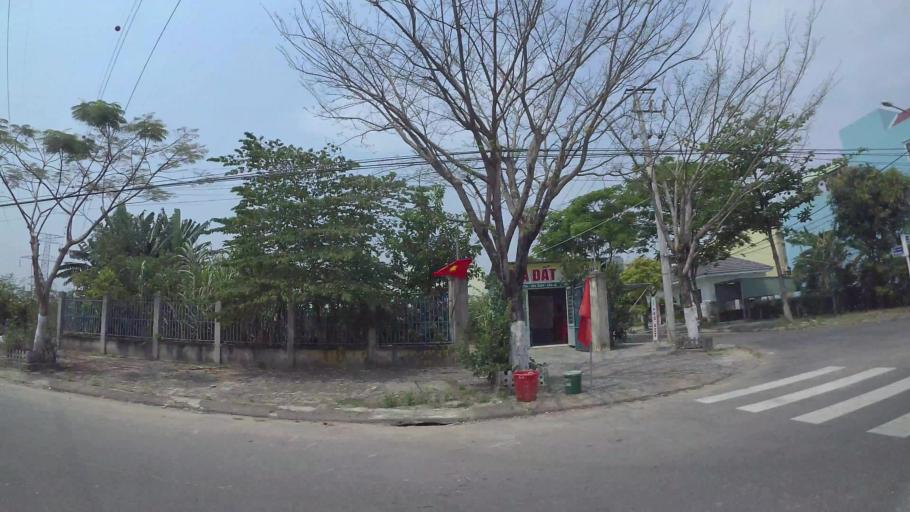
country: VN
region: Da Nang
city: Cam Le
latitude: 16.0013
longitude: 108.2104
